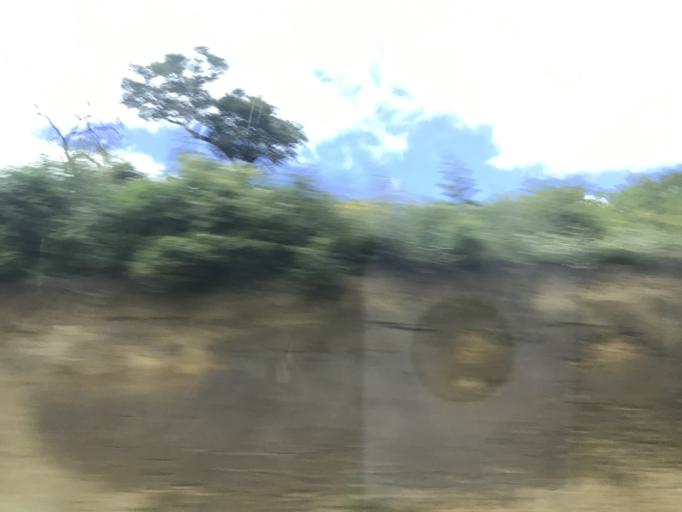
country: GT
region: Chimaltenango
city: El Tejar
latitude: 14.6317
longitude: -90.7917
